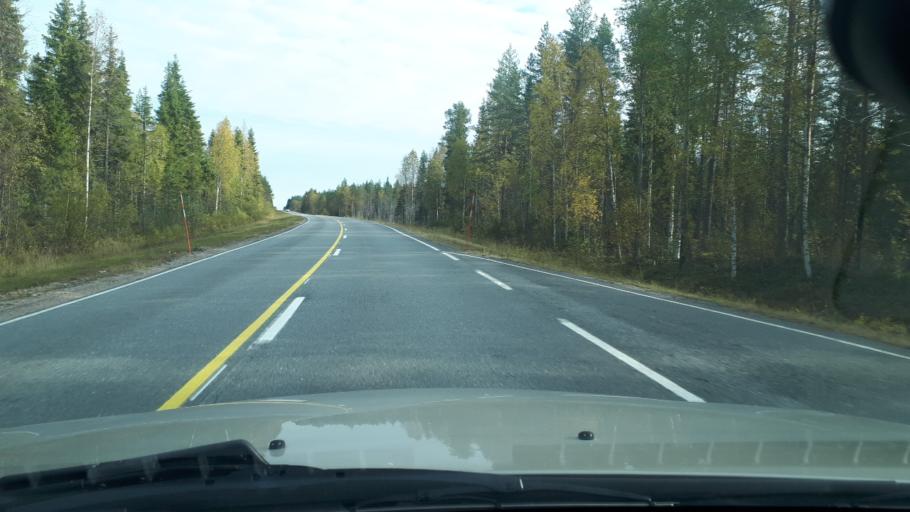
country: FI
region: Lapland
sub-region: Rovaniemi
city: Ranua
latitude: 65.9613
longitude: 26.0700
